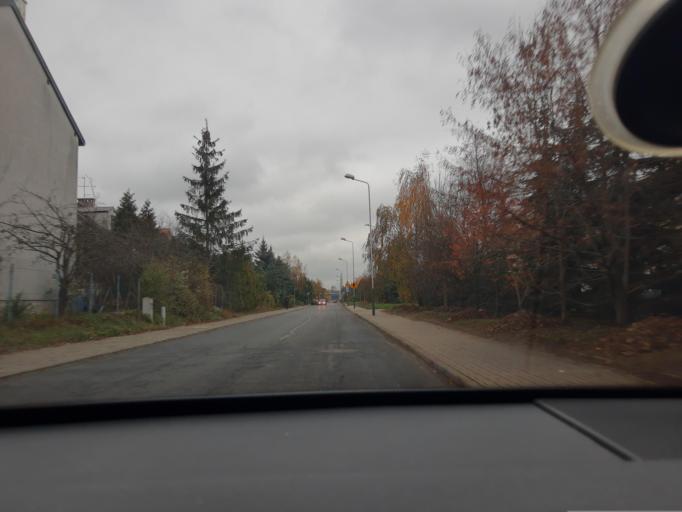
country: PL
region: Lodz Voivodeship
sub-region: Powiat pabianicki
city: Konstantynow Lodzki
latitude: 51.7387
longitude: 19.3750
